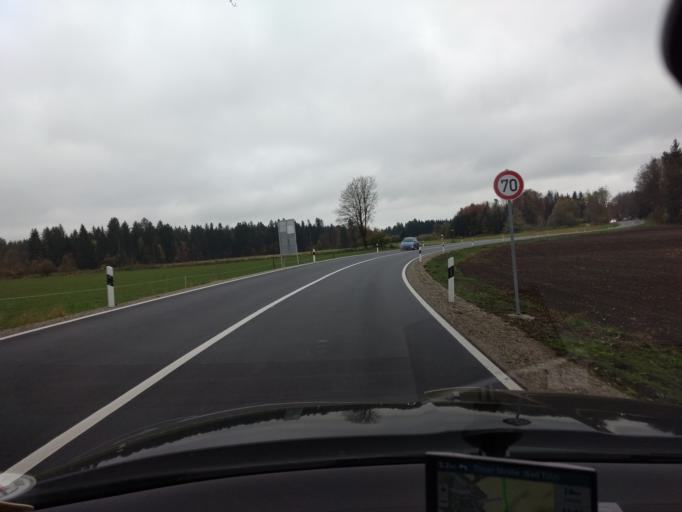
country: DE
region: Bavaria
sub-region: Upper Bavaria
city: Geretsried
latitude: 47.8591
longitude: 11.4687
